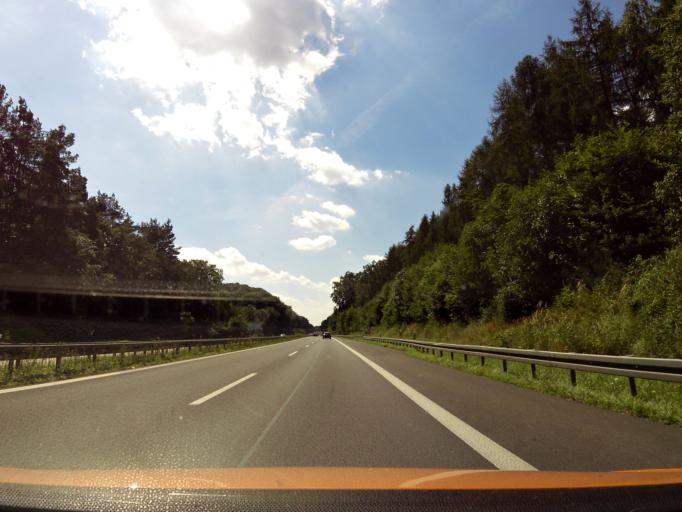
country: DE
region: Brandenburg
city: Gramzow
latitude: 53.2034
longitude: 13.9479
